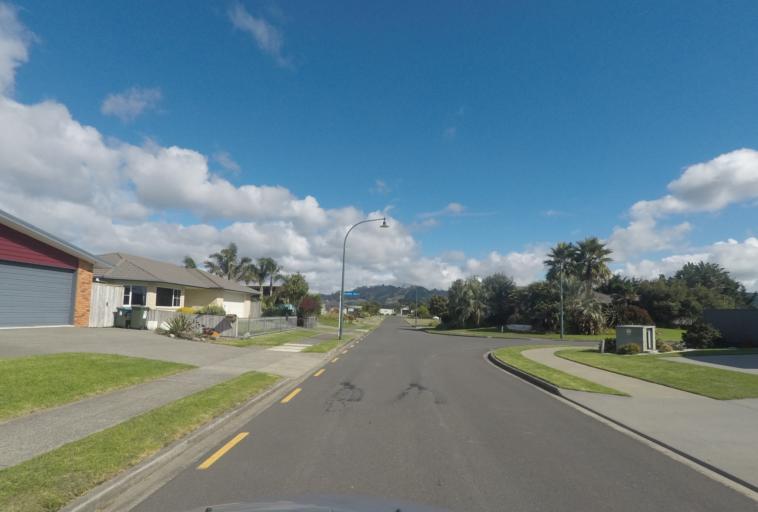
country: NZ
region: Bay of Plenty
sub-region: Western Bay of Plenty District
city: Waihi Beach
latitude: -37.4299
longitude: 175.9557
